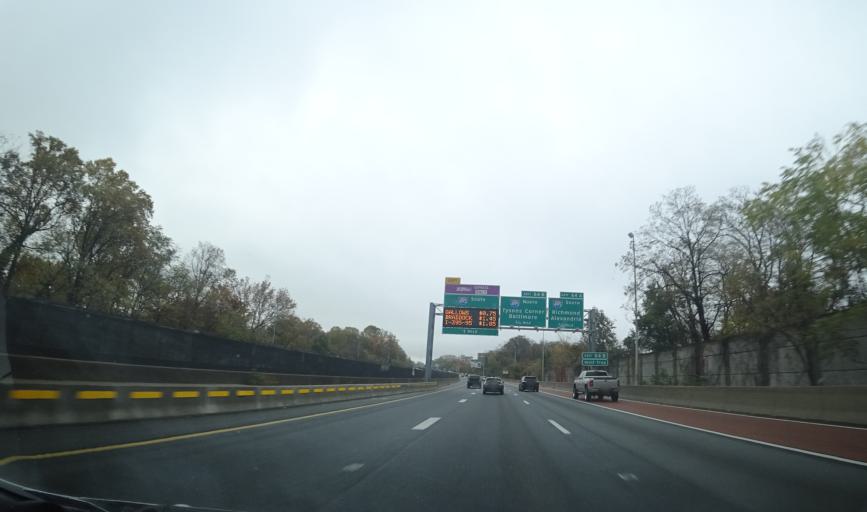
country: US
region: Virginia
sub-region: Fairfax County
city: Merrifield
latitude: 38.8798
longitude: -77.2407
